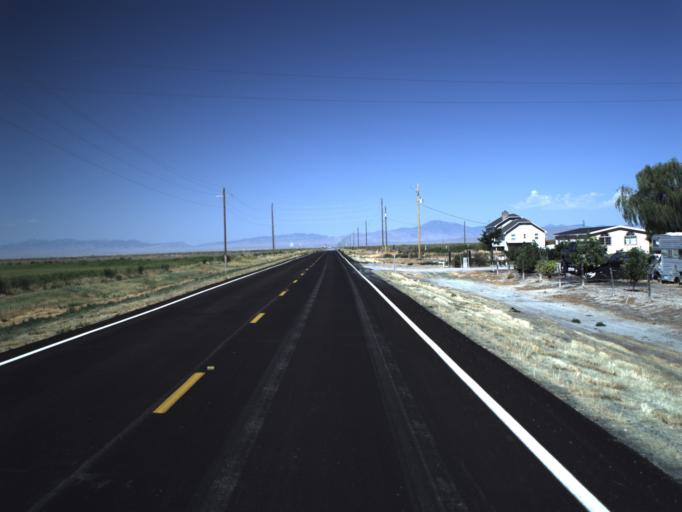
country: US
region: Utah
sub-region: Millard County
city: Delta
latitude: 39.3309
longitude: -112.6811
